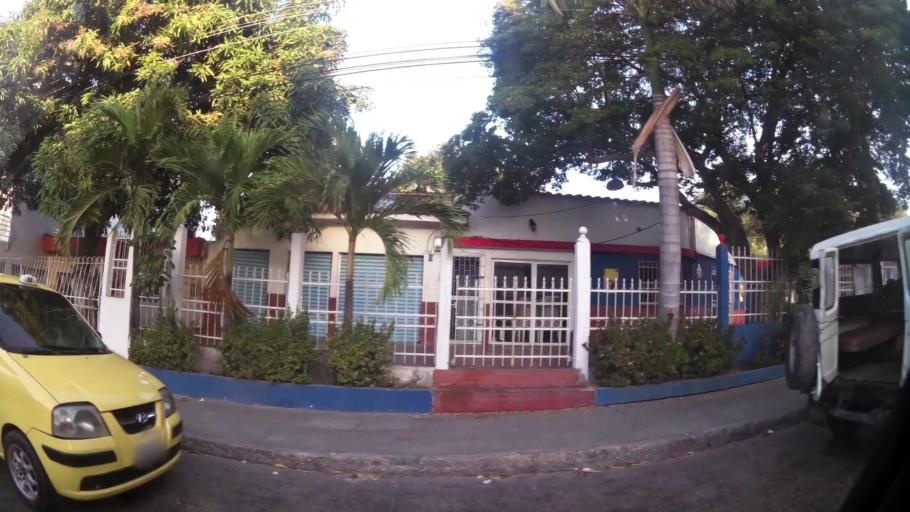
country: CO
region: Bolivar
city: Cartagena
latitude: 10.4278
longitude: -75.5358
